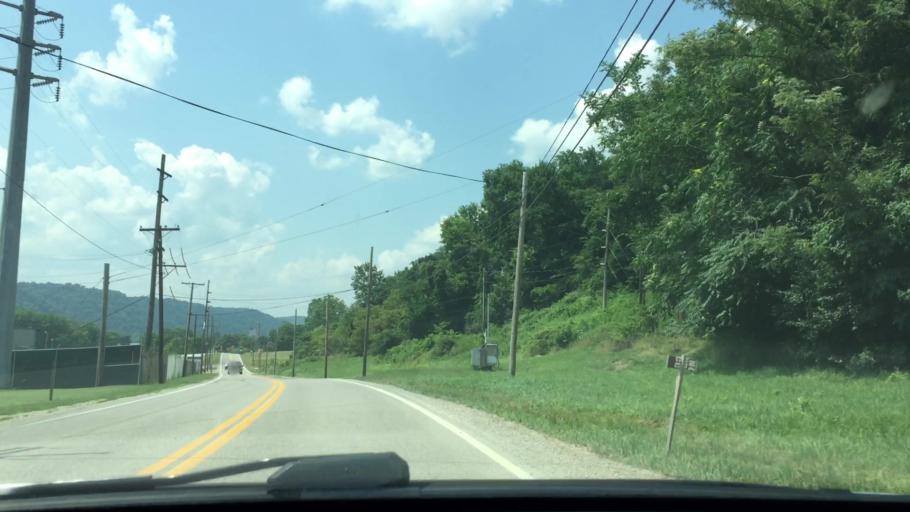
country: US
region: West Virginia
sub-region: Wetzel County
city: New Martinsville
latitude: 39.7305
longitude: -80.8309
